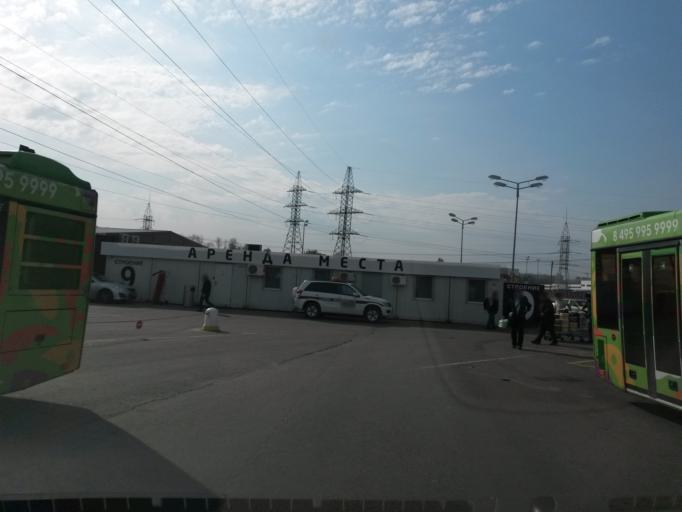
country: RU
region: Moskovskaya
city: Mosrentgen
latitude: 55.5992
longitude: 37.4750
